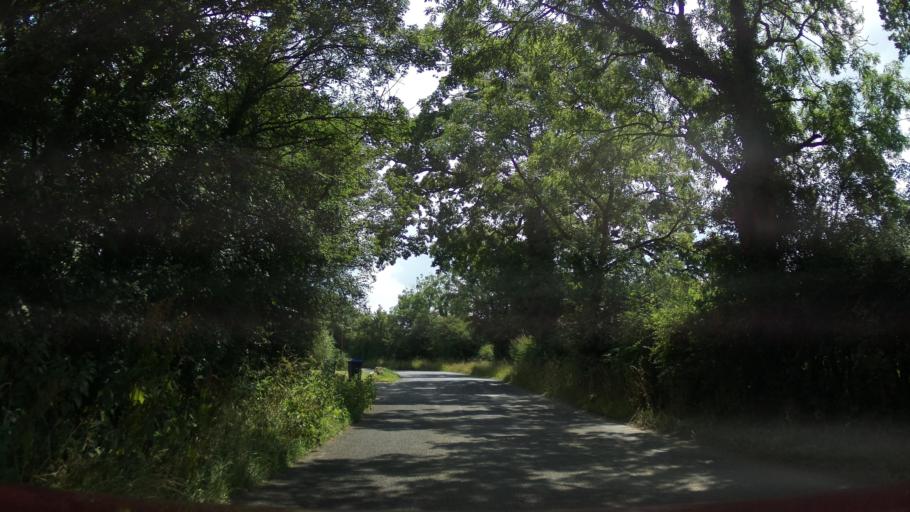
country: GB
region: England
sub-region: Wiltshire
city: Minety
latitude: 51.6014
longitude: -1.9447
